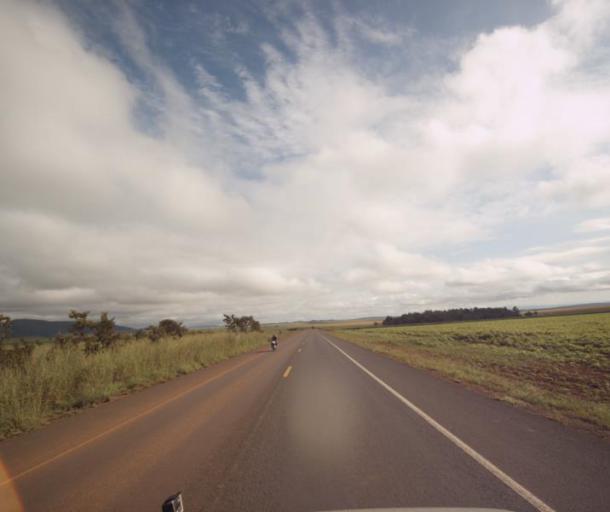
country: BR
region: Goias
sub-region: Padre Bernardo
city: Padre Bernardo
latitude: -15.4230
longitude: -48.6229
